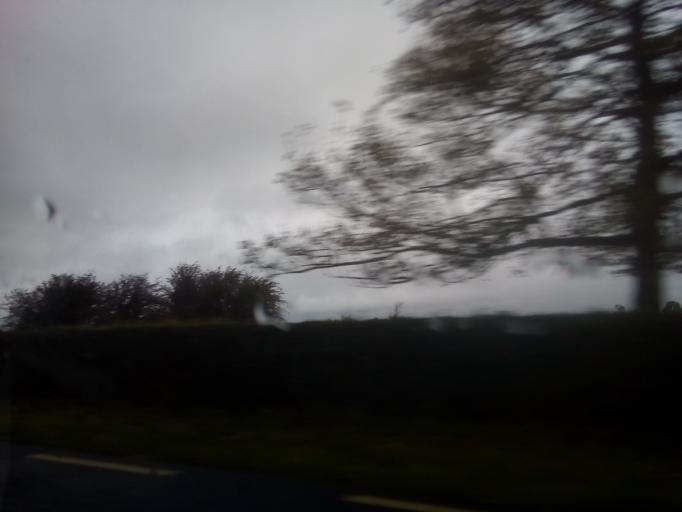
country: IE
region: Connaught
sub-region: Roscommon
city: Castlerea
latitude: 53.8732
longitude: -8.4207
